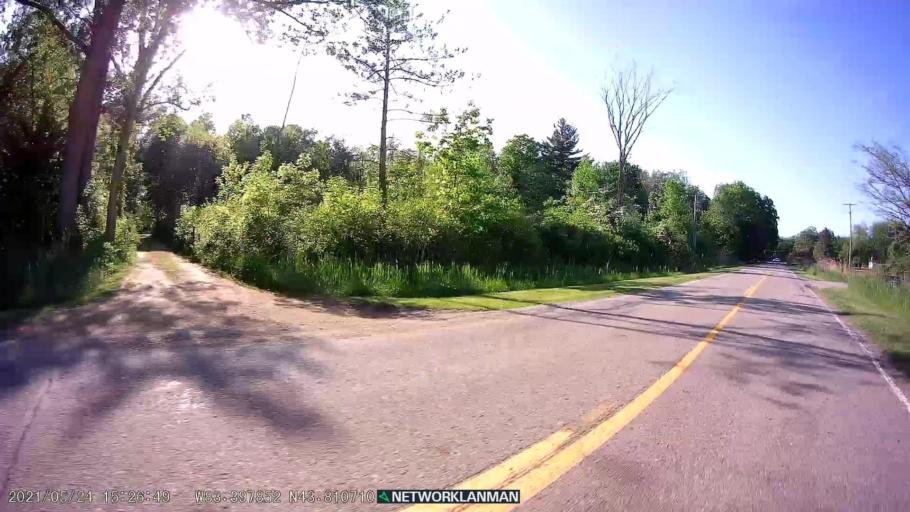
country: US
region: Michigan
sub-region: Huron County
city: Kilmanagh
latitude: 43.8108
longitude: -83.3979
